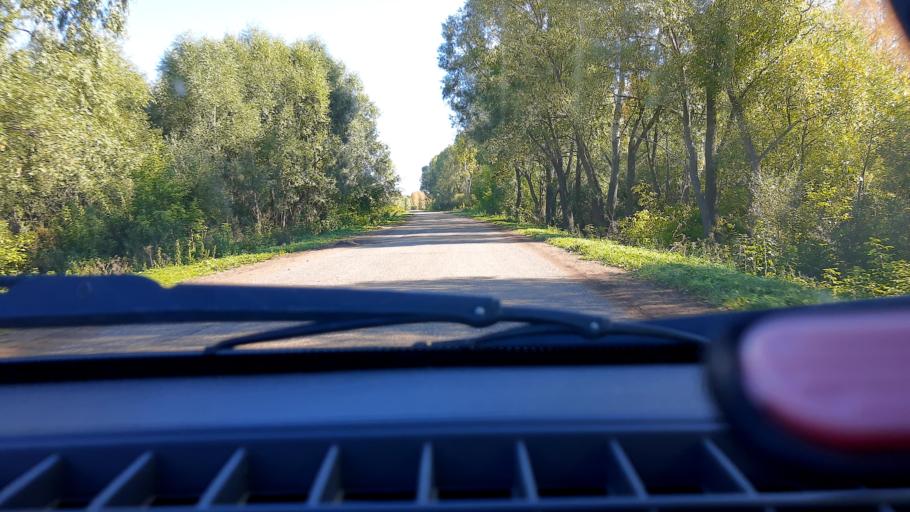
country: RU
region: Bashkortostan
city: Kushnarenkovo
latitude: 55.1002
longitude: 55.5102
